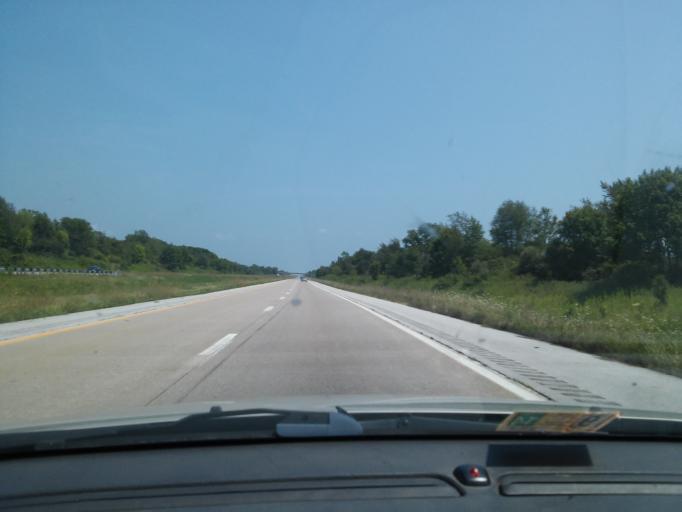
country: US
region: Illinois
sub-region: Scott County
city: Winchester
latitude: 39.6811
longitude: -90.5187
